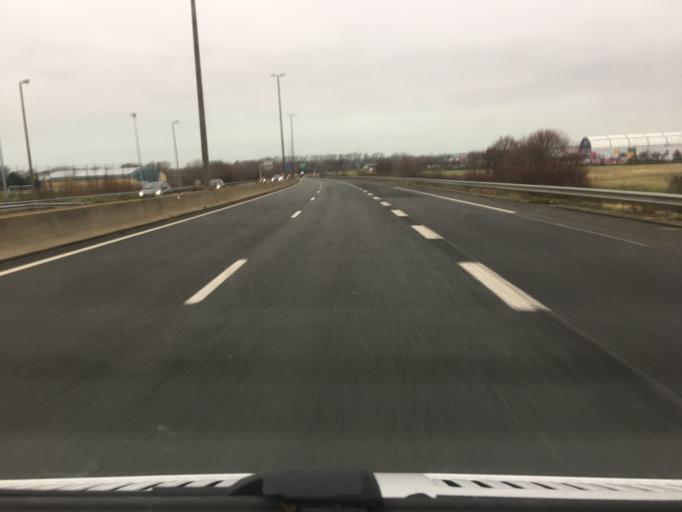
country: FR
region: Nord-Pas-de-Calais
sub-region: Departement du Pas-de-Calais
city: Coquelles
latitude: 50.9294
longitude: 1.8042
